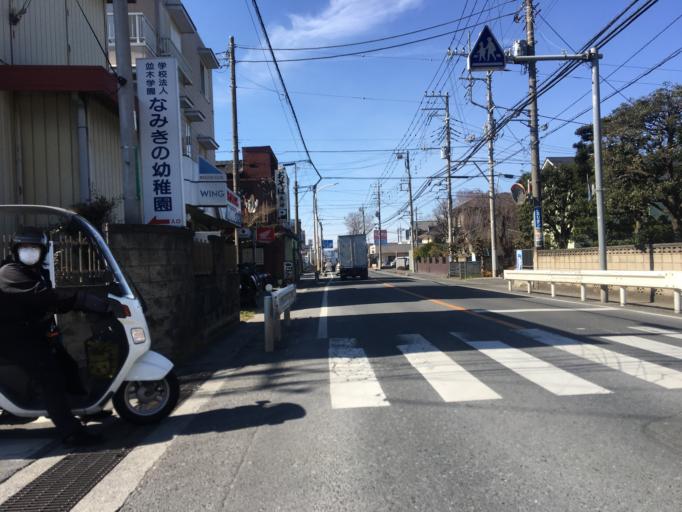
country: JP
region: Saitama
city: Asaka
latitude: 35.8003
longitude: 139.5710
